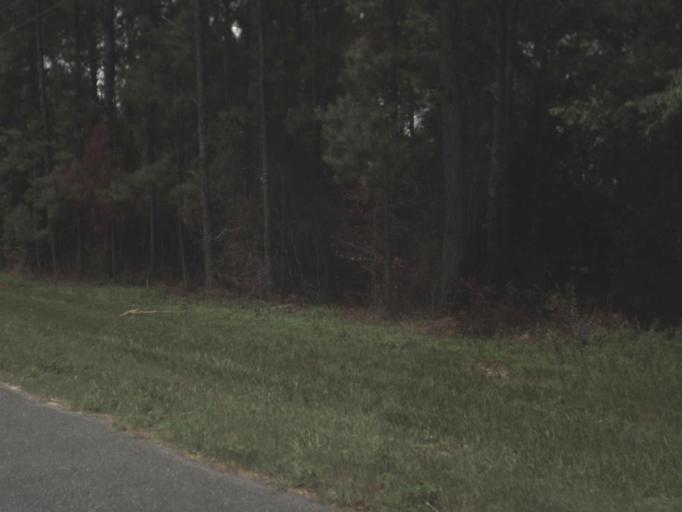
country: US
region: Florida
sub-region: Lafayette County
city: Mayo
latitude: 29.9817
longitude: -82.9341
